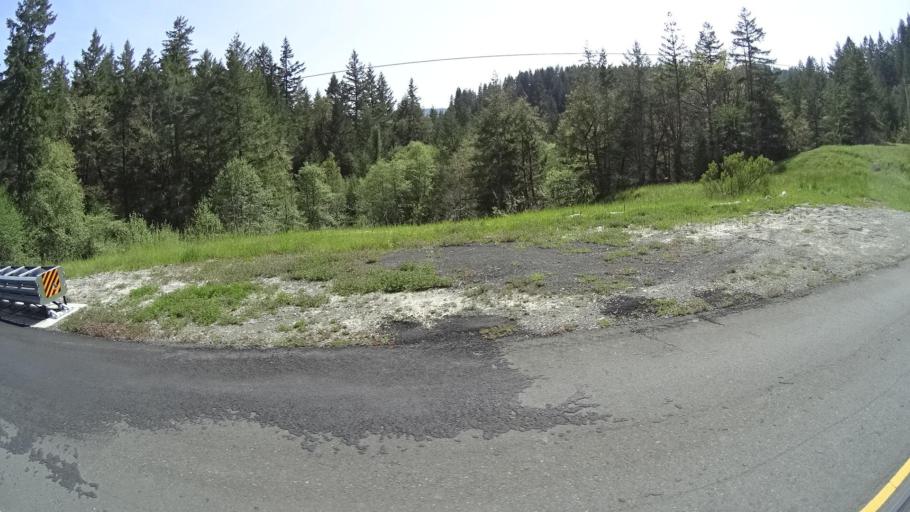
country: US
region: California
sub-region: Humboldt County
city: Redway
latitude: 40.4360
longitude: -123.7698
